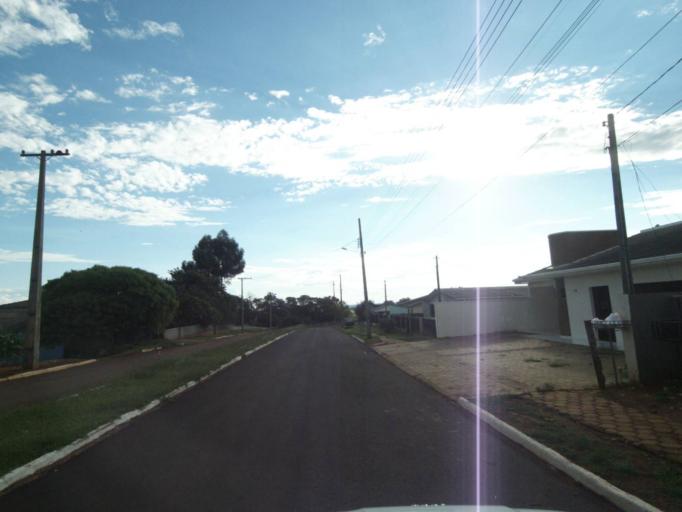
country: BR
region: Parana
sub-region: Laranjeiras Do Sul
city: Laranjeiras do Sul
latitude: -25.4954
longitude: -52.5343
